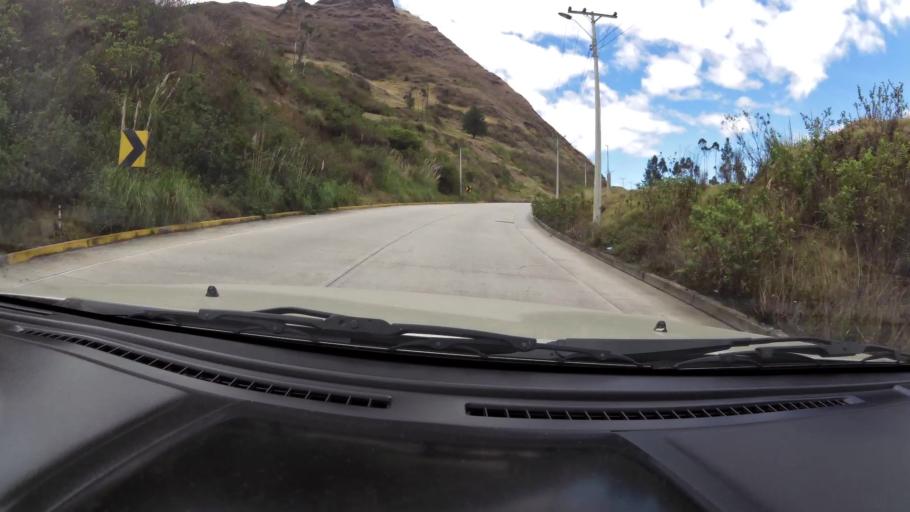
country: EC
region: Azuay
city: Cuenca
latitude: -3.1404
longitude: -79.1221
